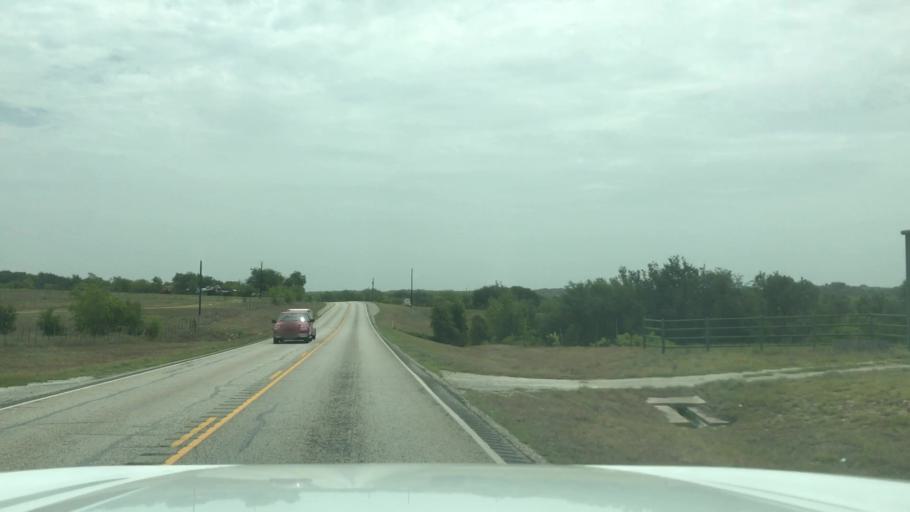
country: US
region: Texas
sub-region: Hamilton County
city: Hico
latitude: 32.0437
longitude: -98.1383
